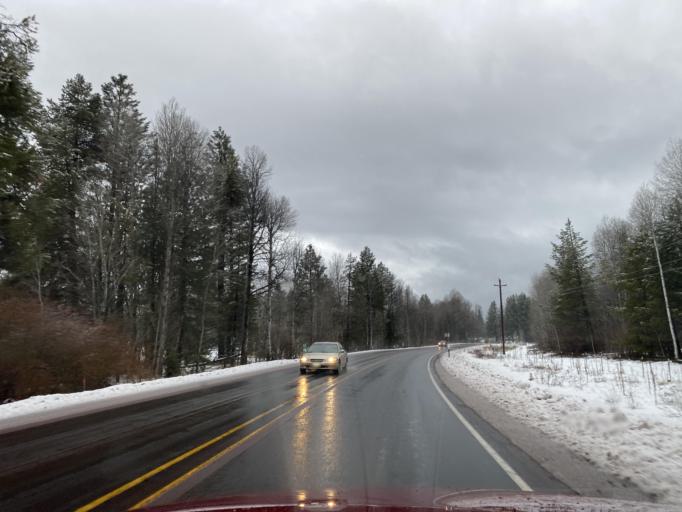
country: US
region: Oregon
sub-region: Klamath County
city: Klamath Falls
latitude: 42.4378
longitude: -122.1194
